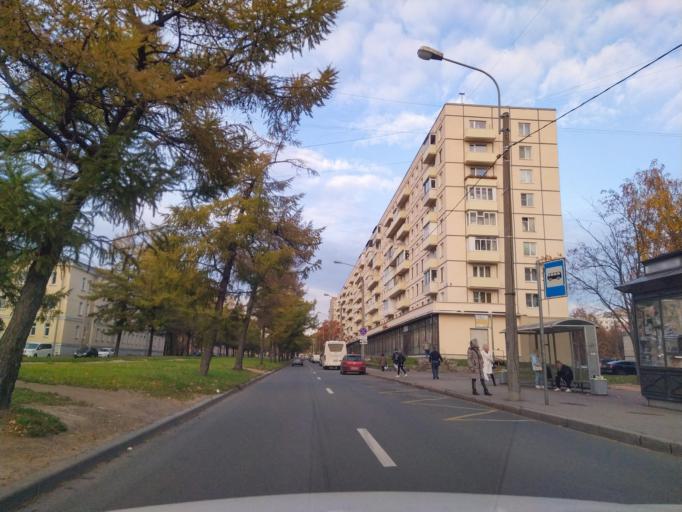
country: RU
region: Leningrad
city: Kalininskiy
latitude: 59.9807
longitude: 30.4070
